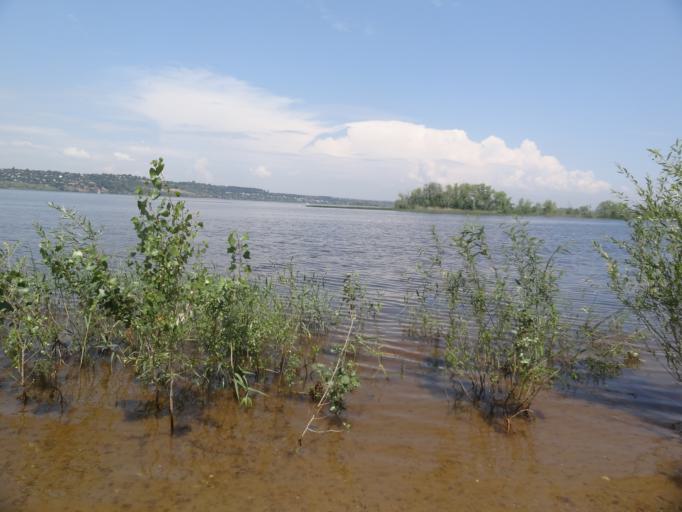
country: RU
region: Saratov
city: Engel's
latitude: 51.5482
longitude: 46.1150
